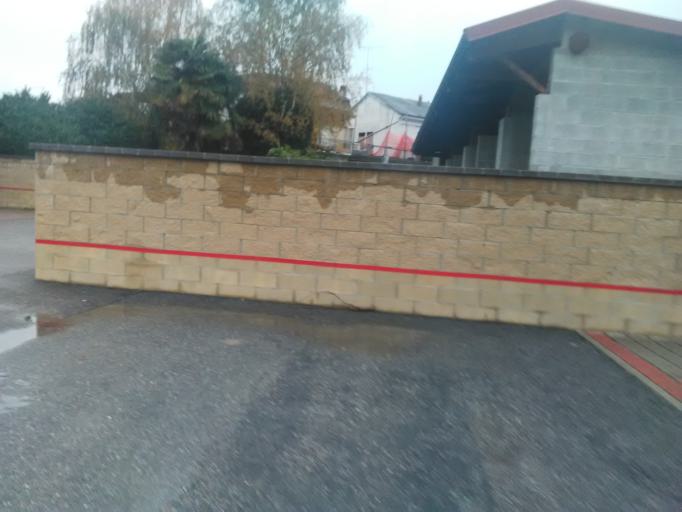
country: IT
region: Piedmont
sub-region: Provincia di Vercelli
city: Cigliano
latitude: 45.3108
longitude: 8.0225
